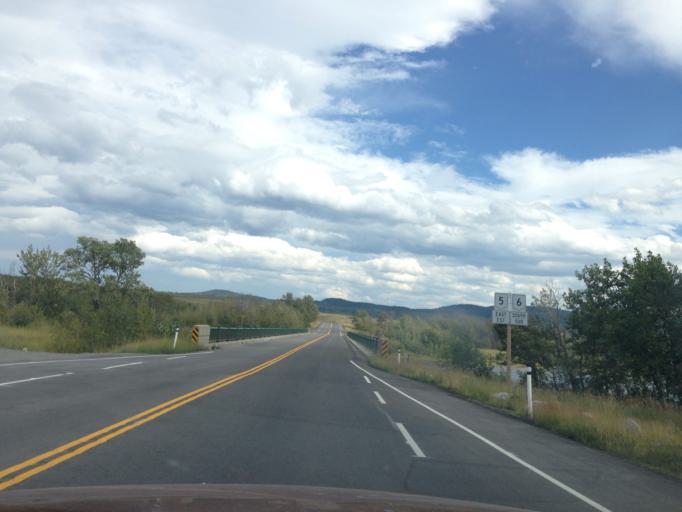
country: CA
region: Alberta
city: Pincher Creek
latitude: 49.1136
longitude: -113.8424
